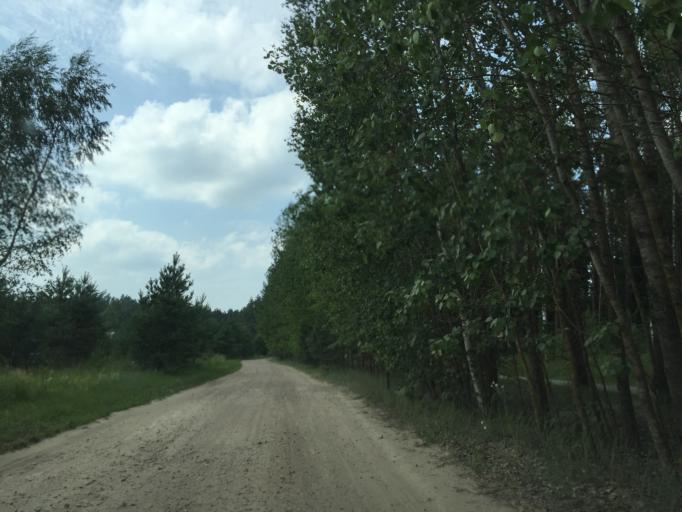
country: LV
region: Olaine
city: Olaine
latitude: 56.7789
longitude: 23.8768
